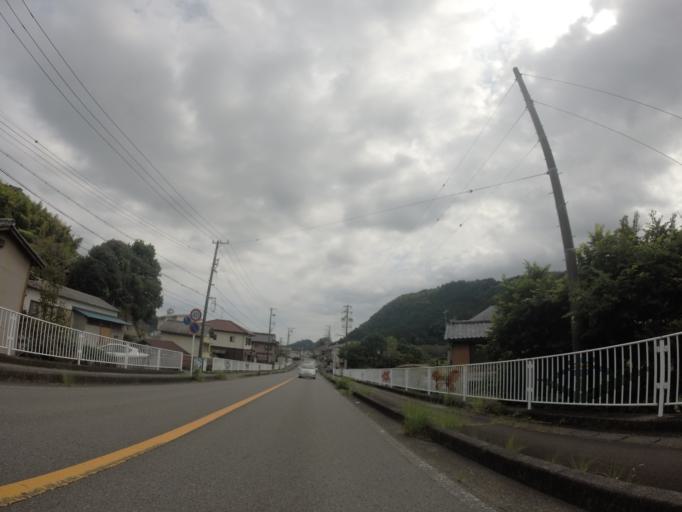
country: JP
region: Shizuoka
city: Fujieda
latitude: 34.8823
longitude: 138.2163
